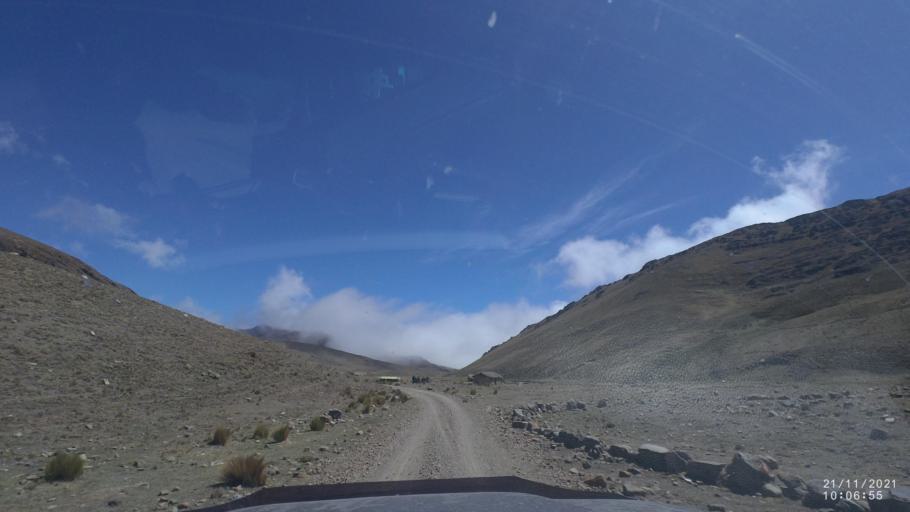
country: BO
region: Cochabamba
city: Cochabamba
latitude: -17.0113
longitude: -66.2843
